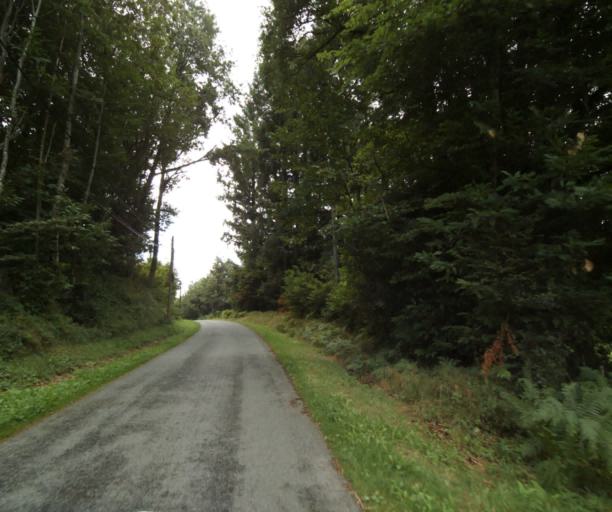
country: FR
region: Limousin
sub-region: Departement de la Correze
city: Sainte-Fortunade
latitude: 45.1996
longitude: 1.8089
